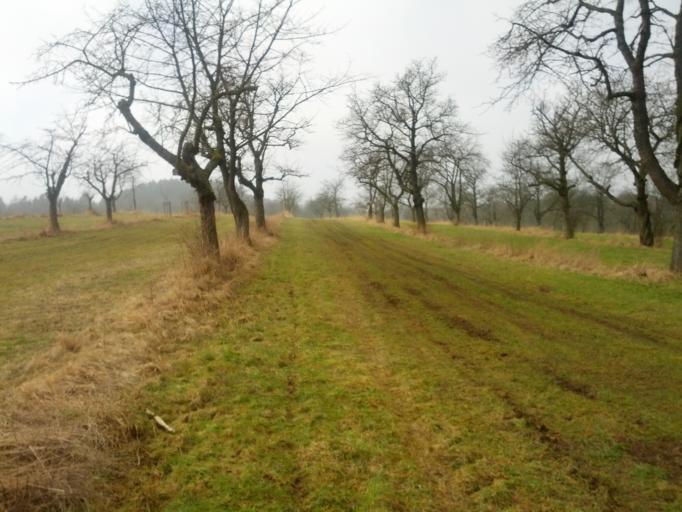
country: DE
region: Thuringia
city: Treffurt
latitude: 51.1425
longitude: 10.2382
